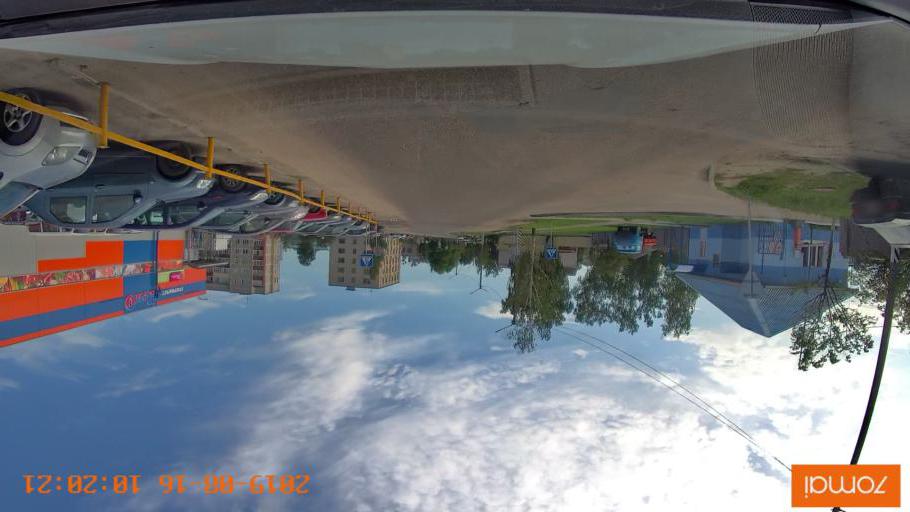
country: BY
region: Mogilev
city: Asipovichy
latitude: 53.3009
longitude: 28.6619
